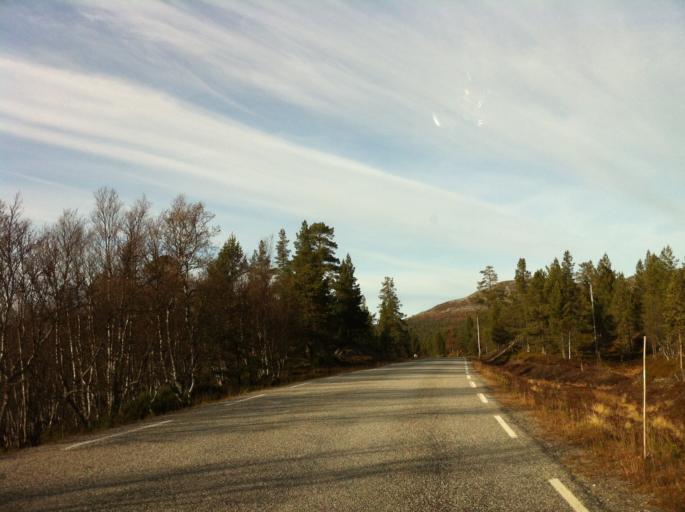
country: NO
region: Hedmark
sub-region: Engerdal
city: Engerdal
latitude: 62.1030
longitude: 12.0256
